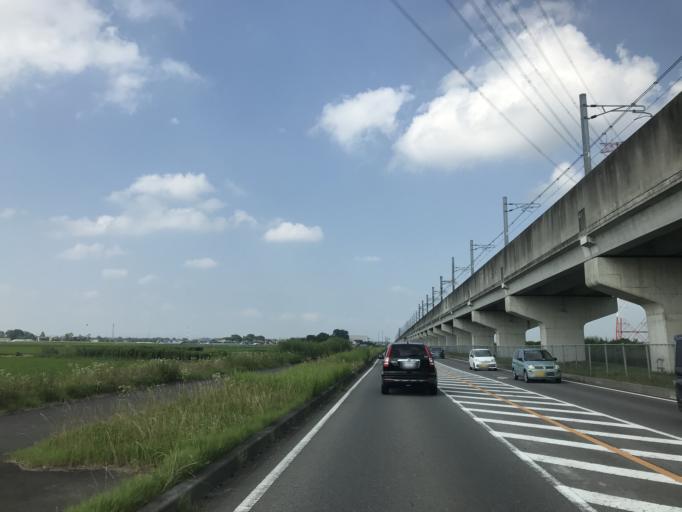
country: JP
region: Ibaraki
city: Moriya
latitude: 35.9684
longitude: 140.0101
